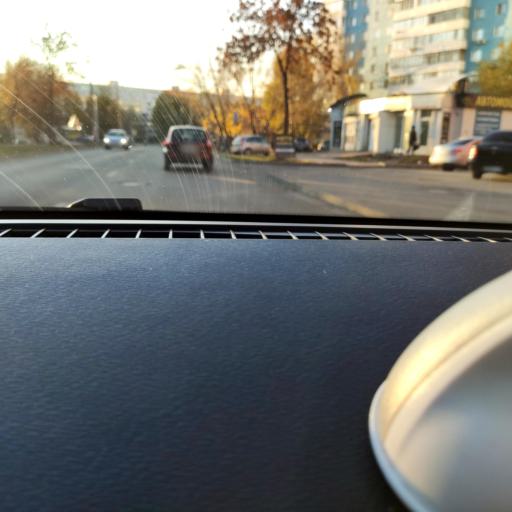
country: RU
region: Samara
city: Samara
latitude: 53.2466
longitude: 50.2119
